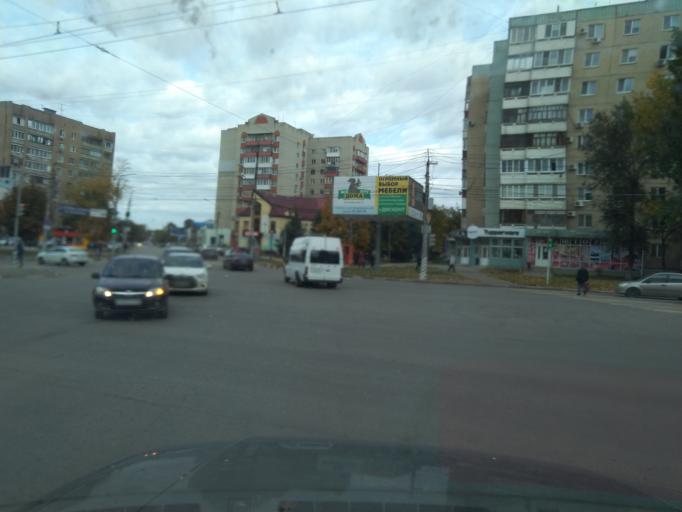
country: RU
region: Saratov
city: Engel's
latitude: 51.4891
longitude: 46.1223
